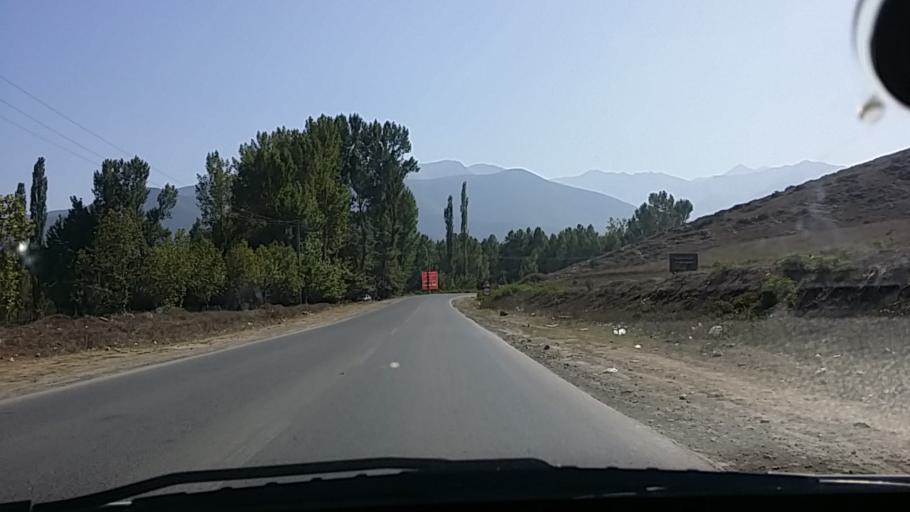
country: IR
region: Mazandaran
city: `Abbasabad
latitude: 36.5330
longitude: 51.1803
